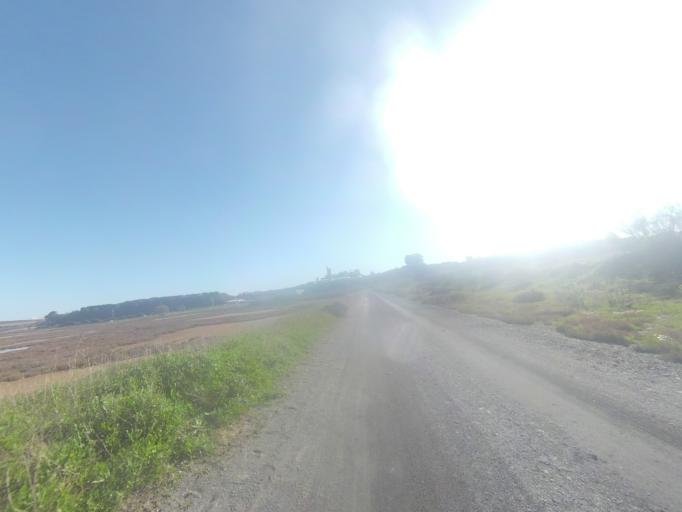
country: ES
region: Andalusia
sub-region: Provincia de Huelva
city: Palos de la Frontera
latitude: 37.2448
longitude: -6.8902
